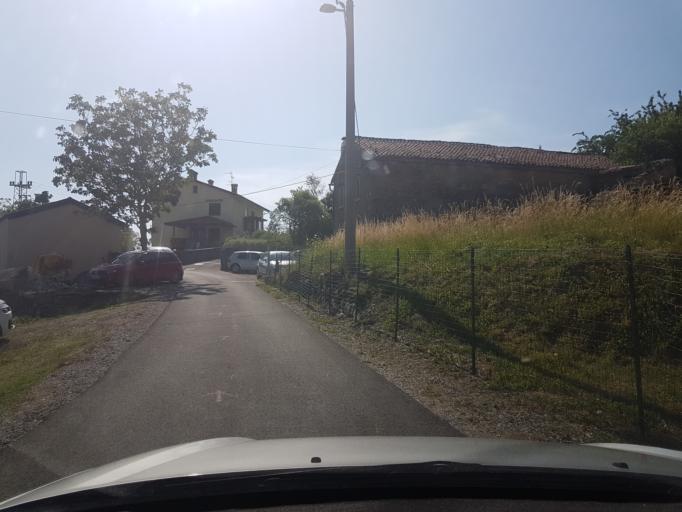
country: SI
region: Vipava
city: Vipava
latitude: 45.7679
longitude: 13.9764
